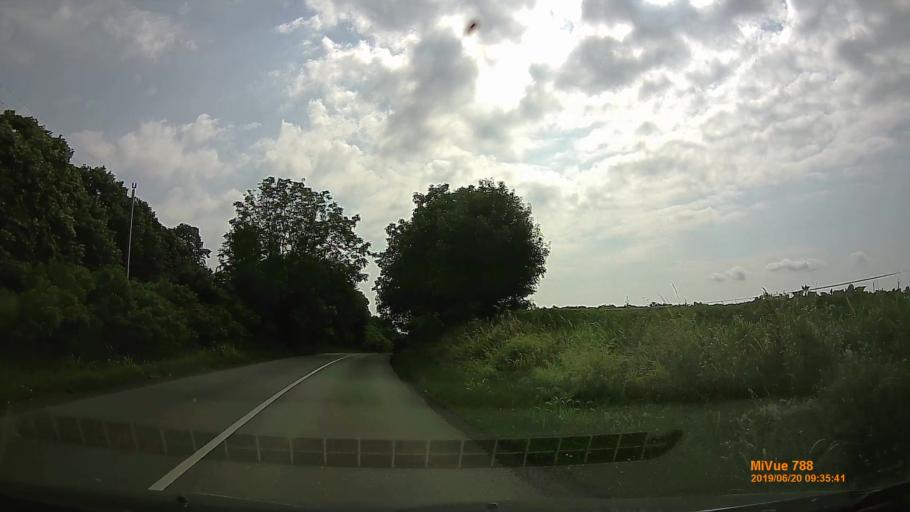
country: HU
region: Baranya
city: Pecsvarad
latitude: 46.1655
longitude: 18.4400
